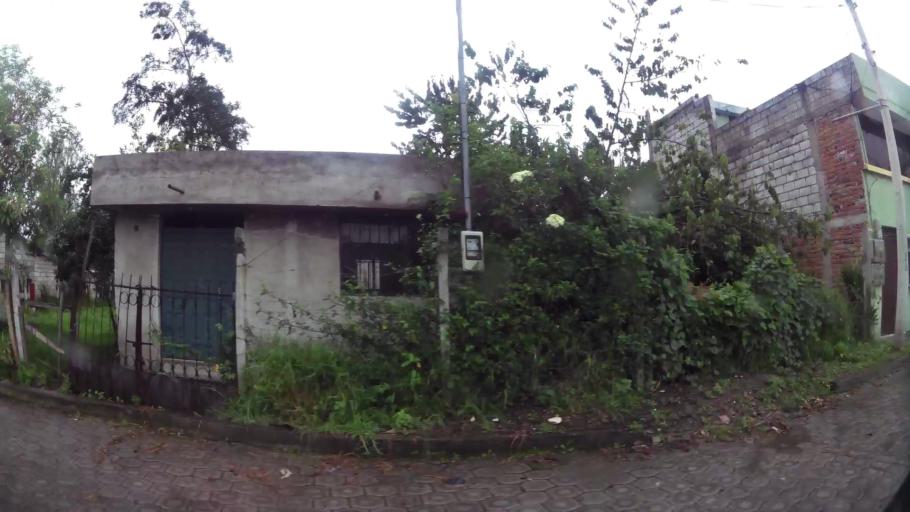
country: EC
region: Pichincha
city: Sangolqui
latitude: -0.2993
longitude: -78.4451
